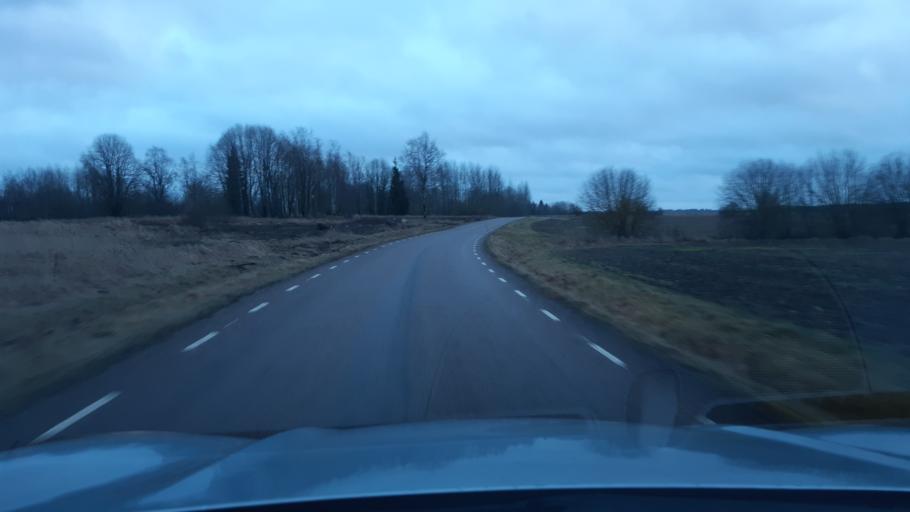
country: EE
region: Raplamaa
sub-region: Rapla vald
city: Rapla
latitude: 59.0068
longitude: 24.7112
